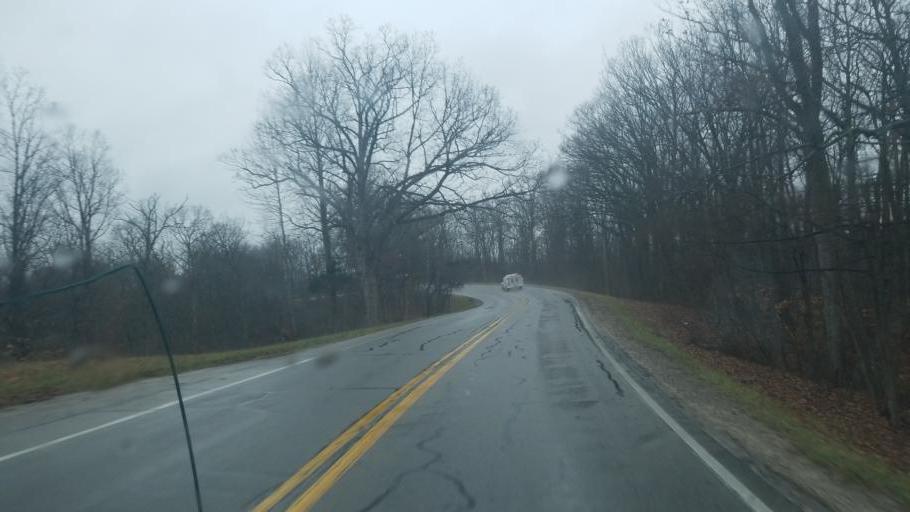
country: US
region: Indiana
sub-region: Brown County
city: Nashville
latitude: 39.1722
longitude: -86.2746
